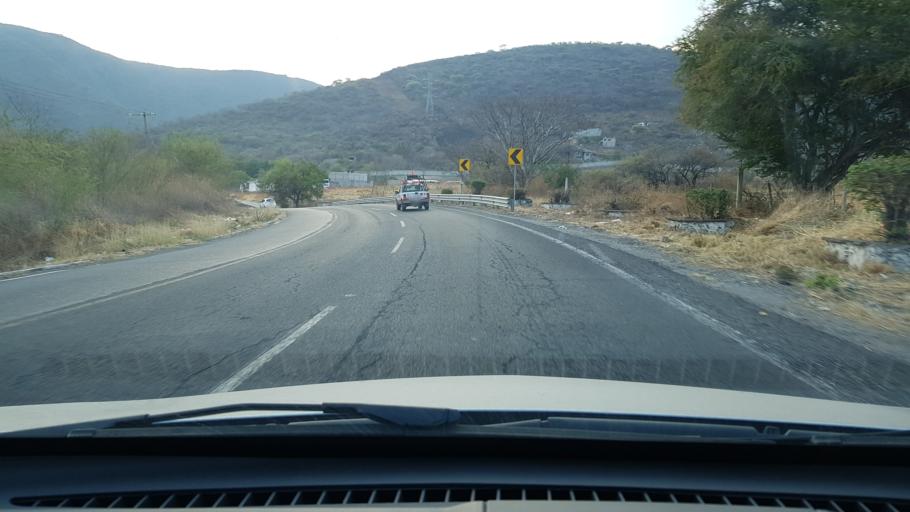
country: MX
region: Morelos
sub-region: Jiutepec
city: Independencia
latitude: 18.8591
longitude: -99.1040
